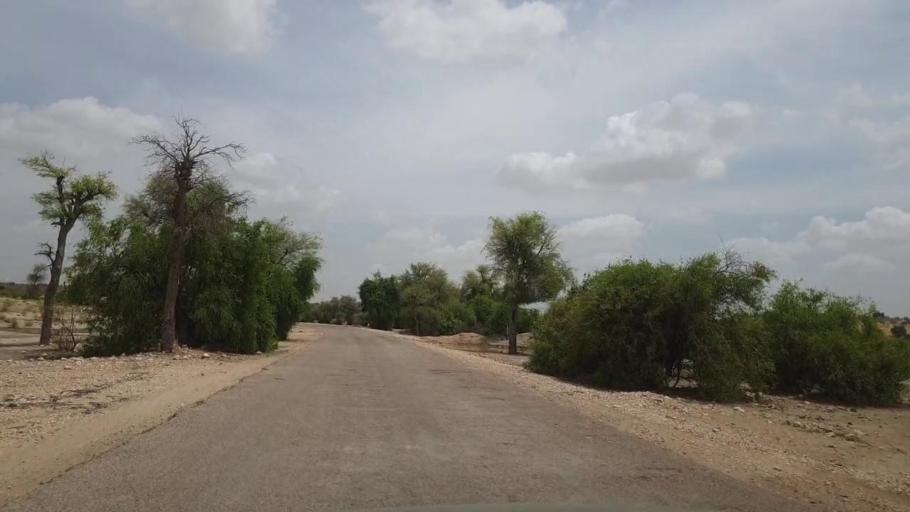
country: PK
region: Sindh
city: Kot Diji
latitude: 27.1809
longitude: 69.1738
